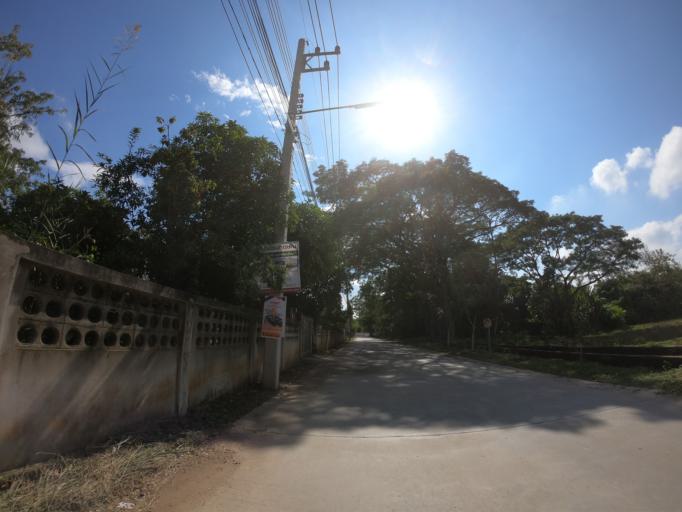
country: TH
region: Chiang Mai
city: San Sai
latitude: 18.8440
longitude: 99.0616
